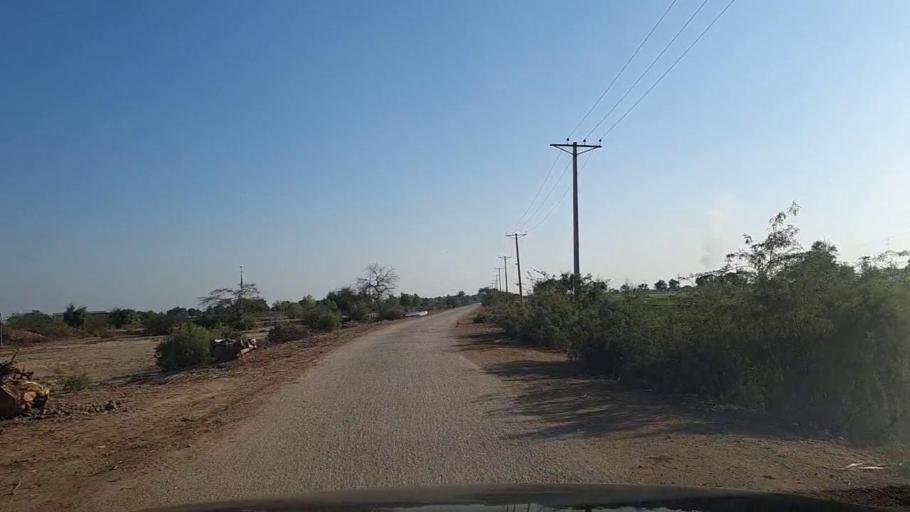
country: PK
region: Sindh
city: Nawabshah
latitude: 26.2127
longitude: 68.3733
